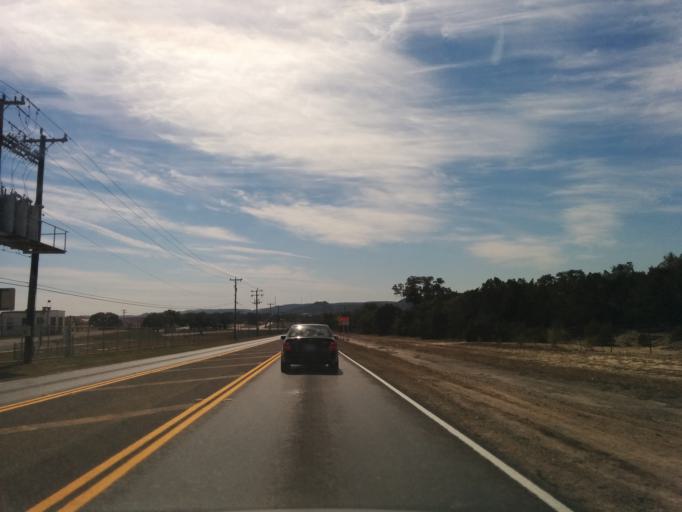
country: US
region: Texas
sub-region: Bexar County
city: Cross Mountain
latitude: 29.6837
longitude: -98.6315
